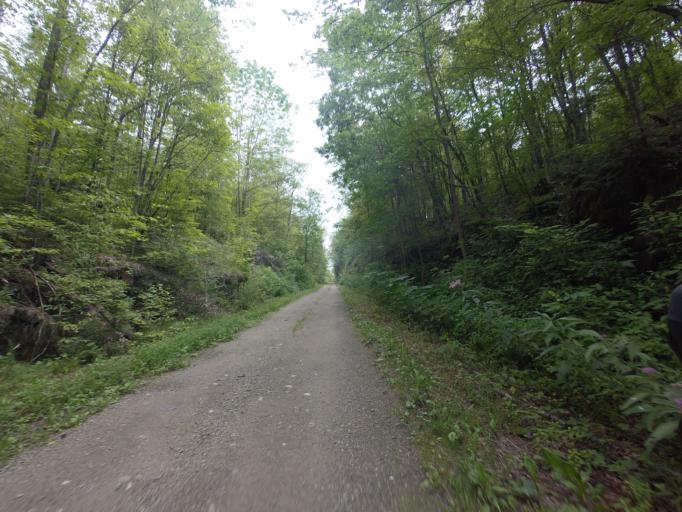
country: CA
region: Ontario
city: Perth
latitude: 44.8235
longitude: -76.5621
